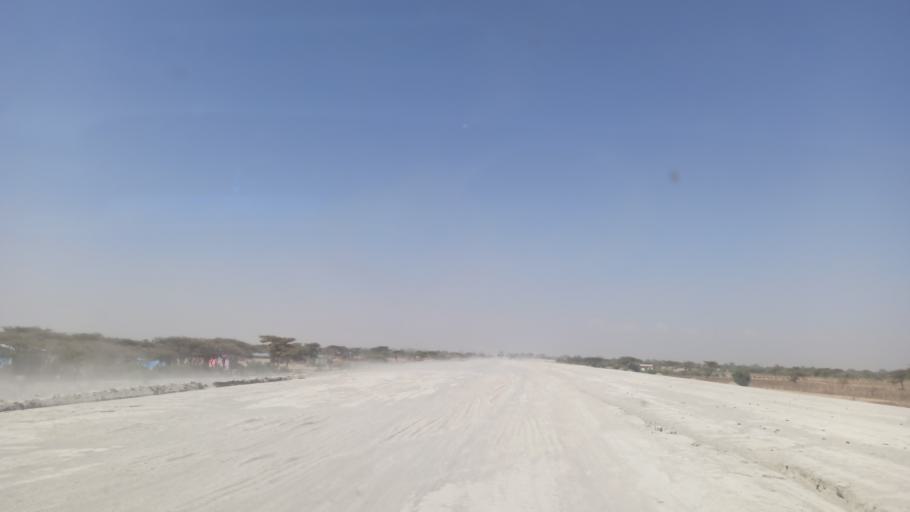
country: ET
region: Oromiya
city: Ziway
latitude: 7.6911
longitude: 38.6587
